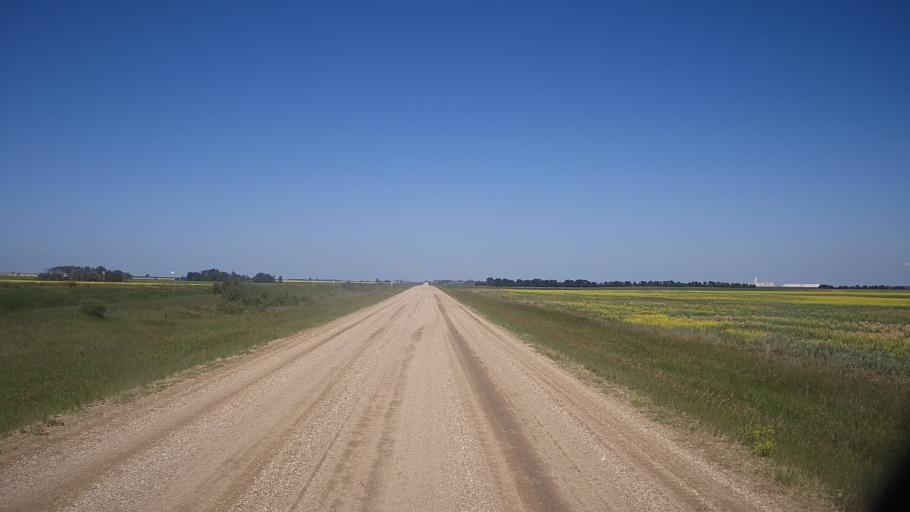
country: CA
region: Saskatchewan
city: Watrous
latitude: 51.8729
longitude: -105.9990
